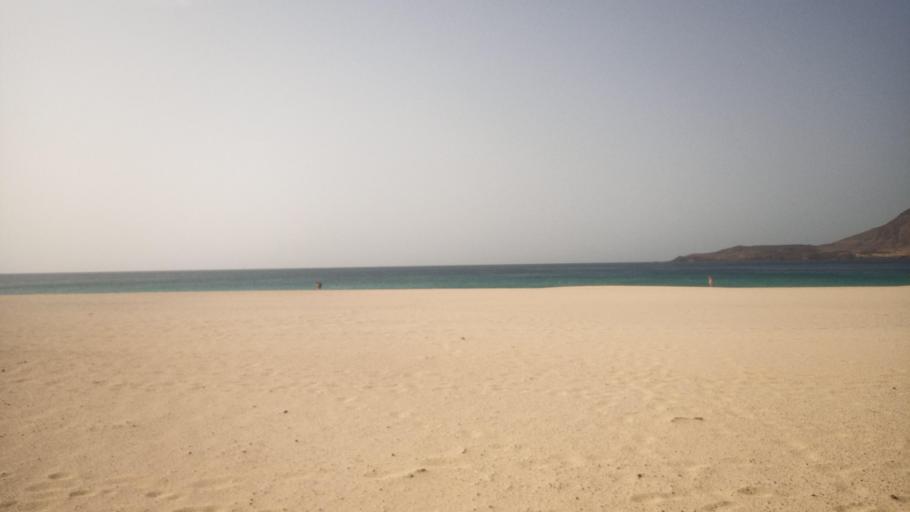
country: ES
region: Canary Islands
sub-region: Provincia de Las Palmas
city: Haria
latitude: 29.2763
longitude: -13.5148
